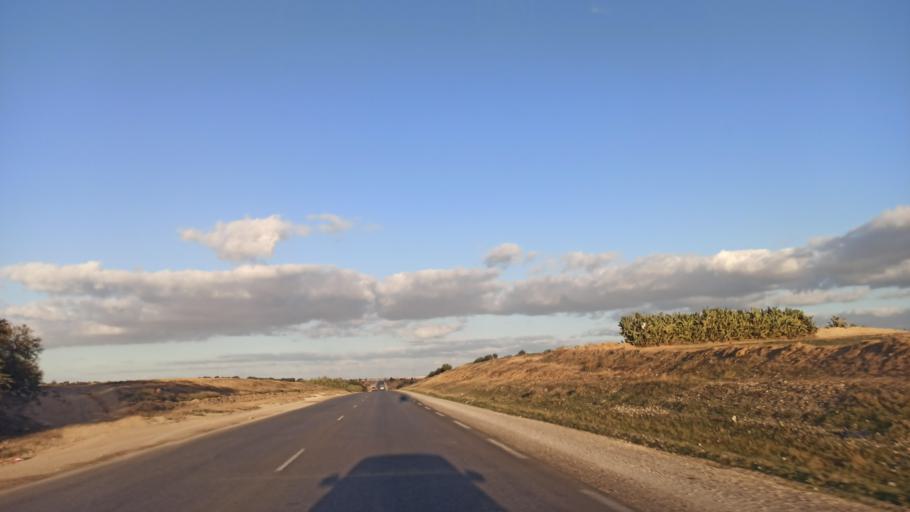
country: TN
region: Al Qayrawan
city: Sbikha
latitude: 35.8829
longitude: 10.2332
